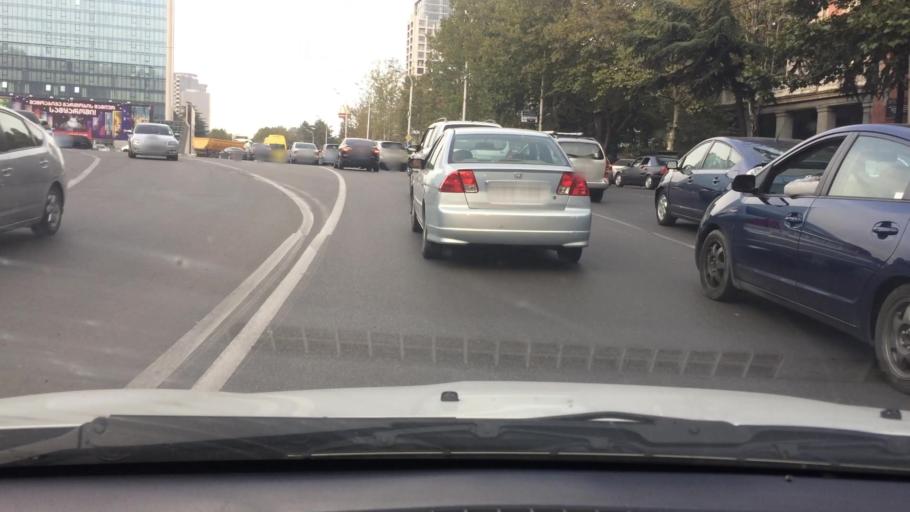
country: GE
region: T'bilisi
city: Tbilisi
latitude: 41.7171
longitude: 44.7789
